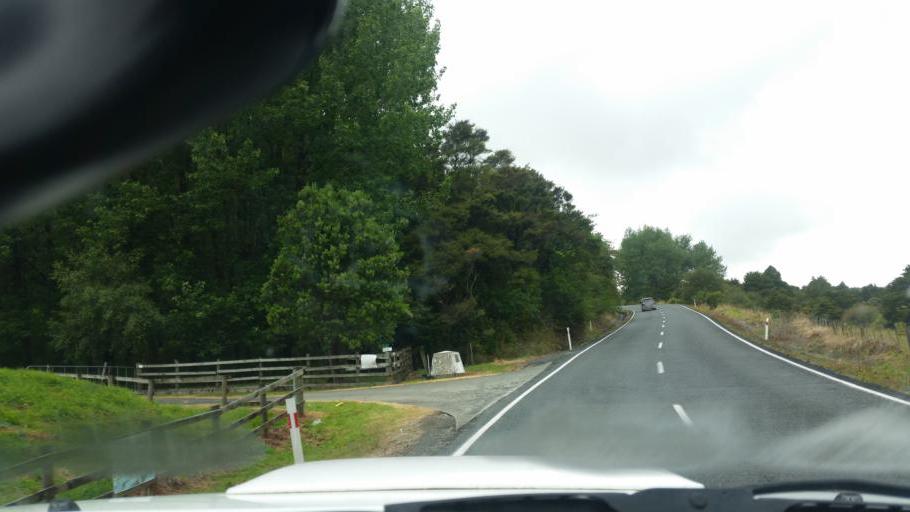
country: NZ
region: Auckland
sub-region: Auckland
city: Wellsford
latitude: -36.1545
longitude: 174.4642
